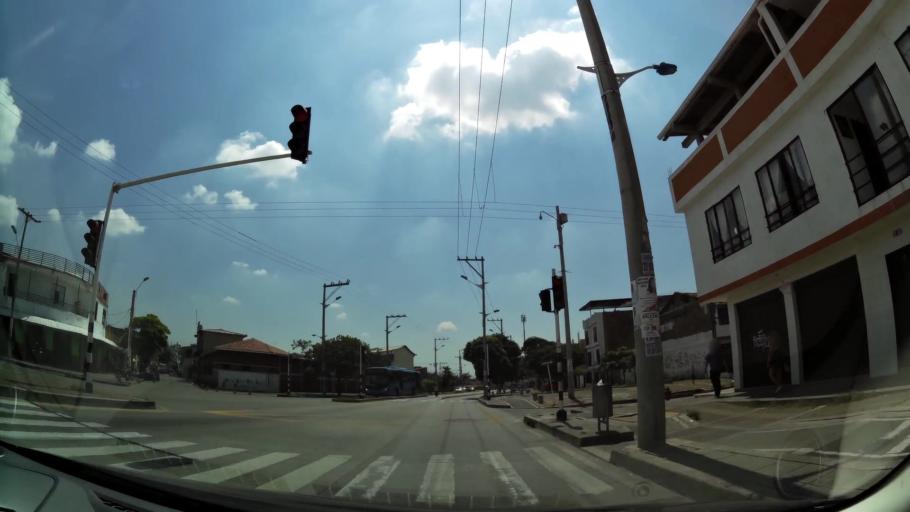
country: CO
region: Valle del Cauca
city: Cali
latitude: 3.4396
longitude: -76.5224
